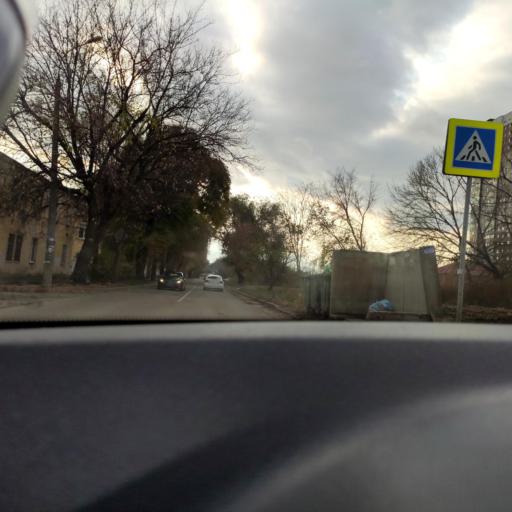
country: RU
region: Samara
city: Samara
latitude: 53.2170
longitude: 50.1951
